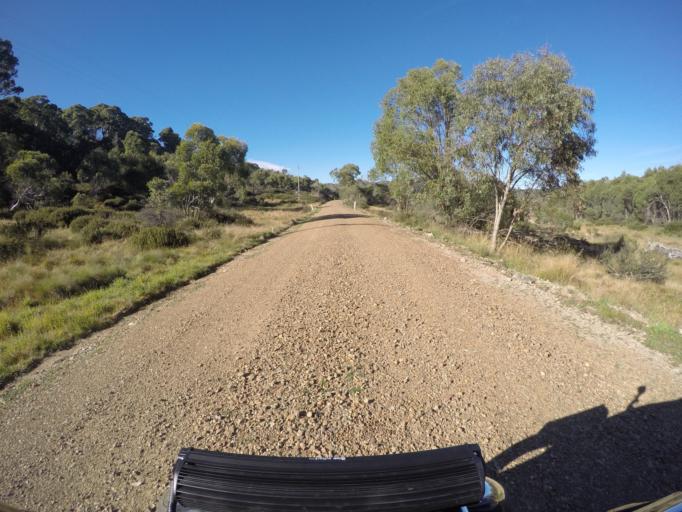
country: AU
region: New South Wales
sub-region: Snowy River
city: Jindabyne
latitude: -36.0508
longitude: 148.2814
